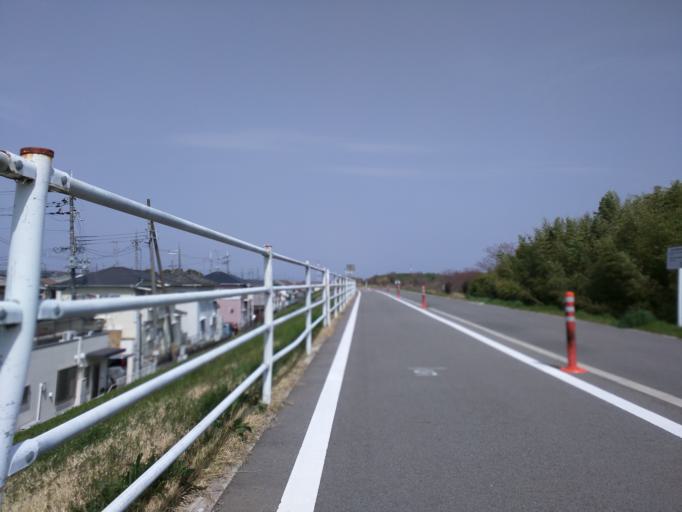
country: JP
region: Kyoto
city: Tanabe
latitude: 34.7841
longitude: 135.7997
